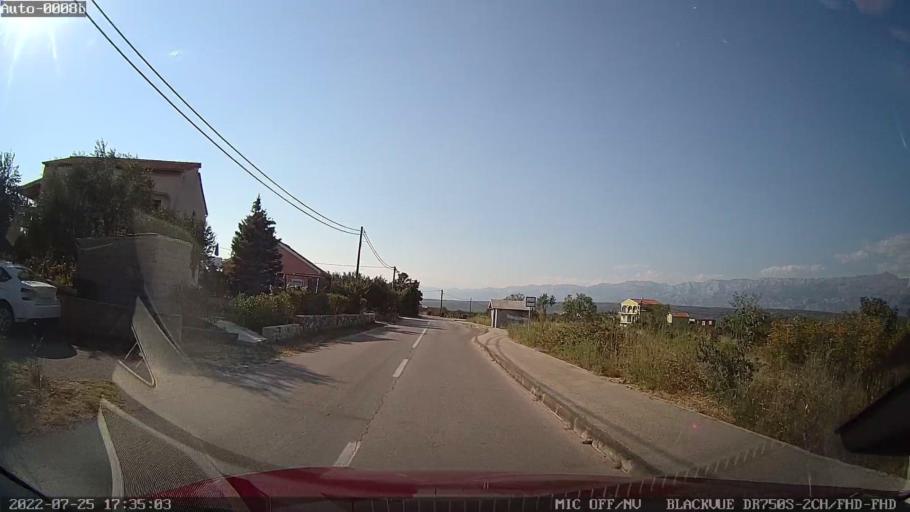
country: HR
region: Zadarska
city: Posedarje
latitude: 44.1878
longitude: 15.4739
